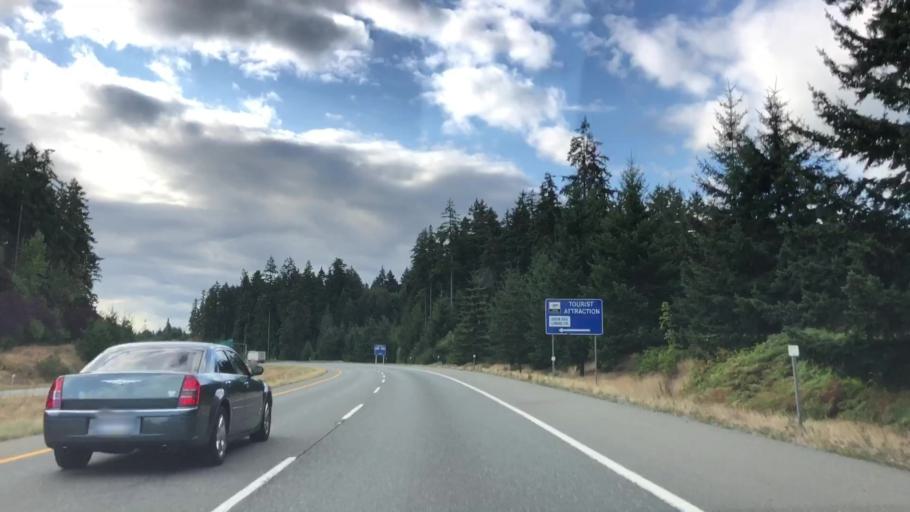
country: CA
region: British Columbia
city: Nanaimo
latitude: 49.2118
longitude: -124.0436
